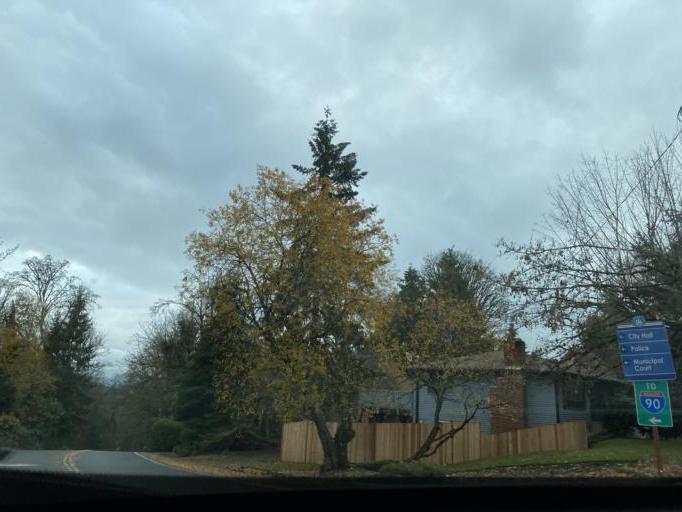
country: US
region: Washington
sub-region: King County
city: Mercer Island
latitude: 47.5746
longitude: -122.2188
